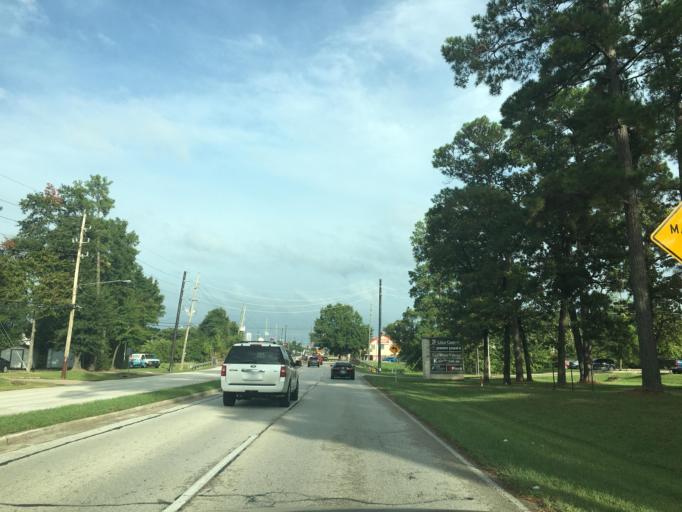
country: US
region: Texas
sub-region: Montgomery County
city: Oak Ridge North
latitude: 30.1265
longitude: -95.4572
